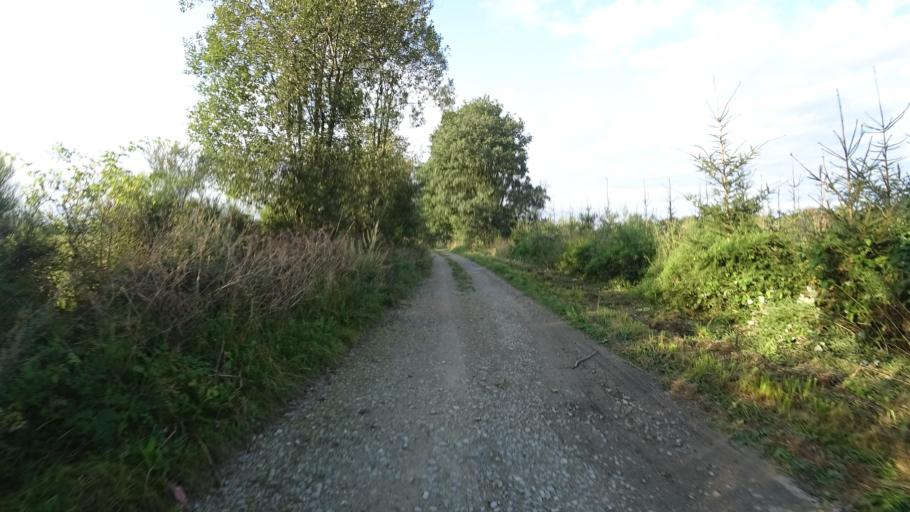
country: BE
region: Wallonia
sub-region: Province du Luxembourg
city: Neufchateau
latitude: 49.8686
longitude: 5.3745
